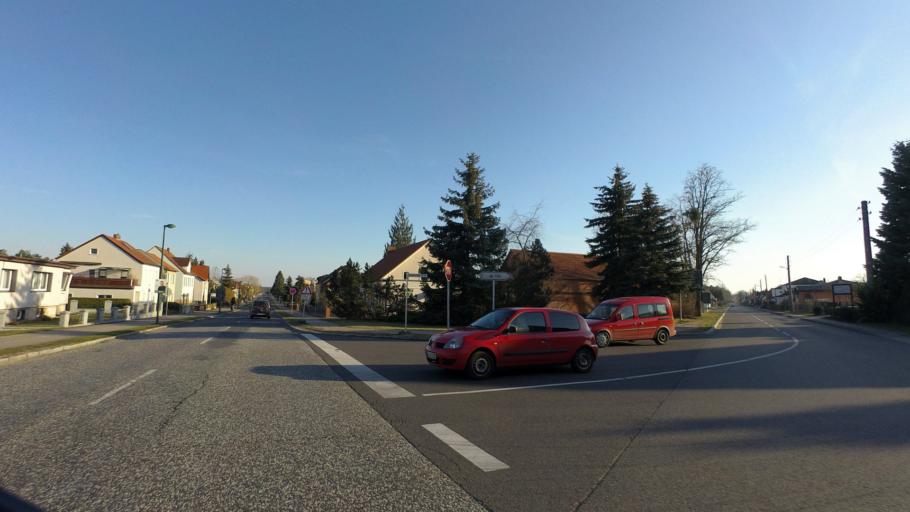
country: DE
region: Brandenburg
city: Britz
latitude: 52.8797
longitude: 13.8170
